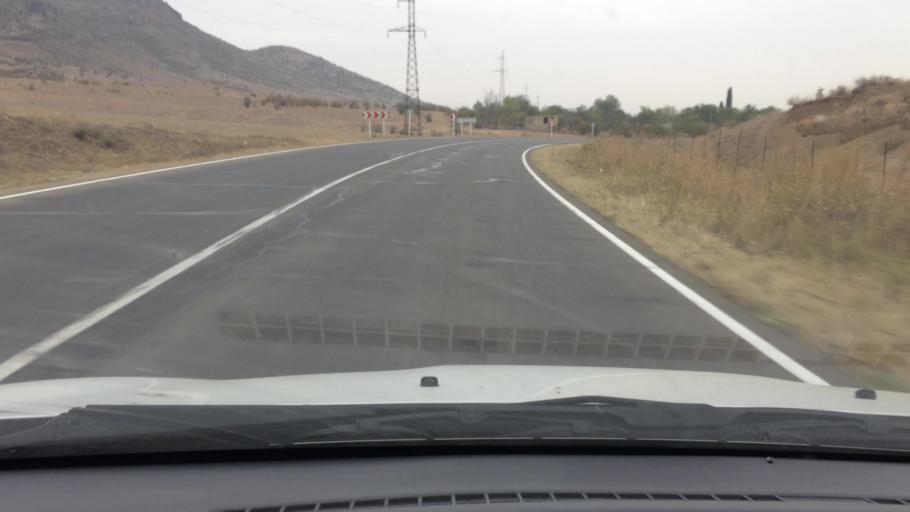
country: GE
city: Naghvarevi
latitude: 41.3529
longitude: 44.8212
